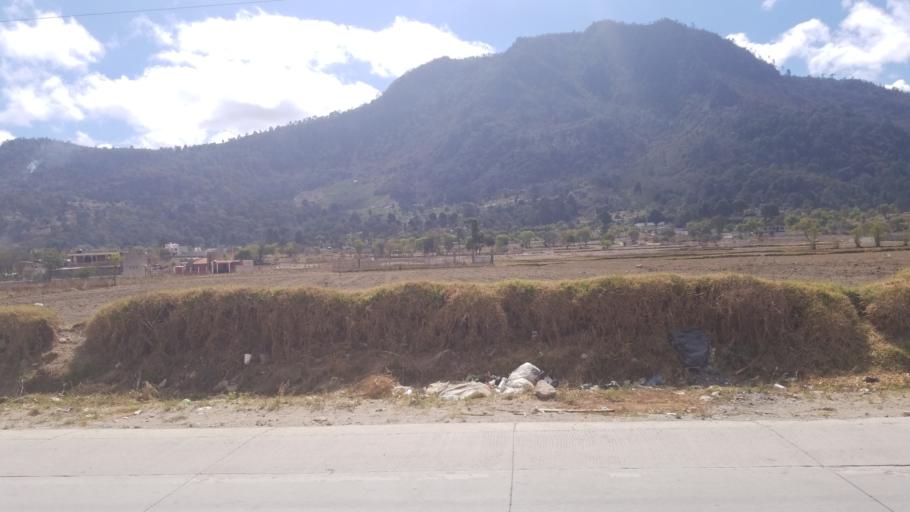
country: GT
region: Quetzaltenango
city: Quetzaltenango
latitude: 14.8056
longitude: -91.5413
